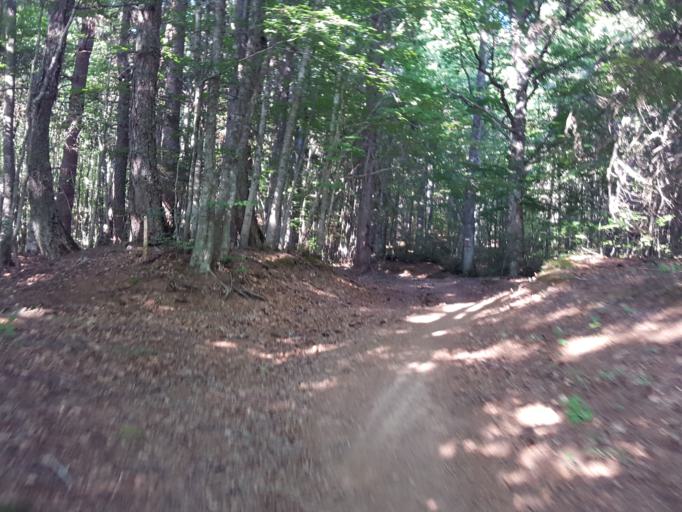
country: IT
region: Tuscany
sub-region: Provincia di Pistoia
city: Abetone
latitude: 44.1550
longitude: 10.6754
